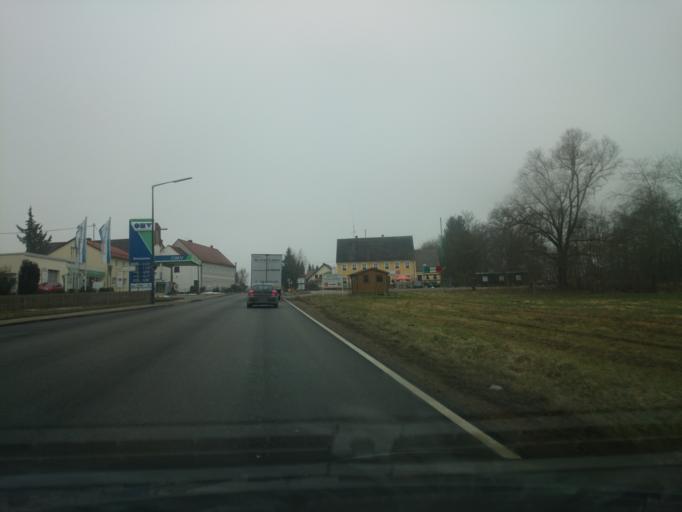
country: DE
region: Bavaria
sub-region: Upper Bavaria
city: Pornbach
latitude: 48.6029
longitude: 11.4246
